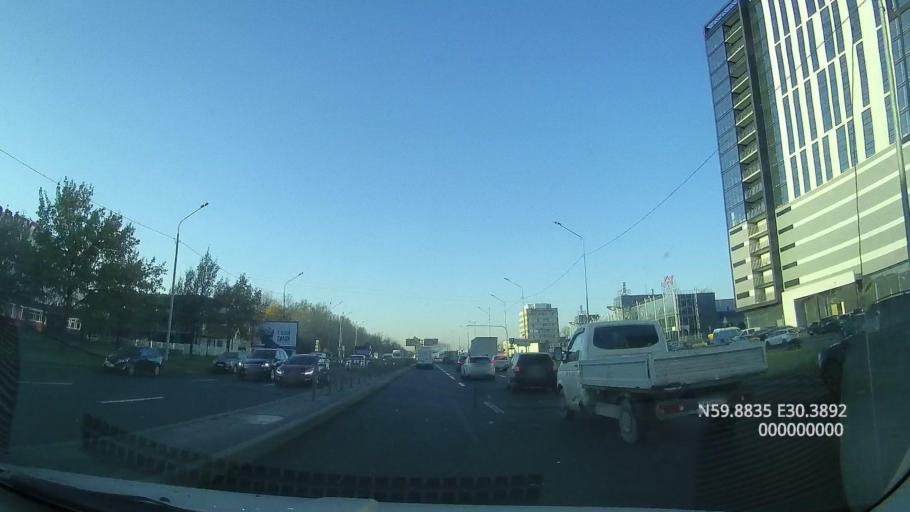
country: RU
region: St.-Petersburg
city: Kupchino
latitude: 59.8837
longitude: 30.3886
